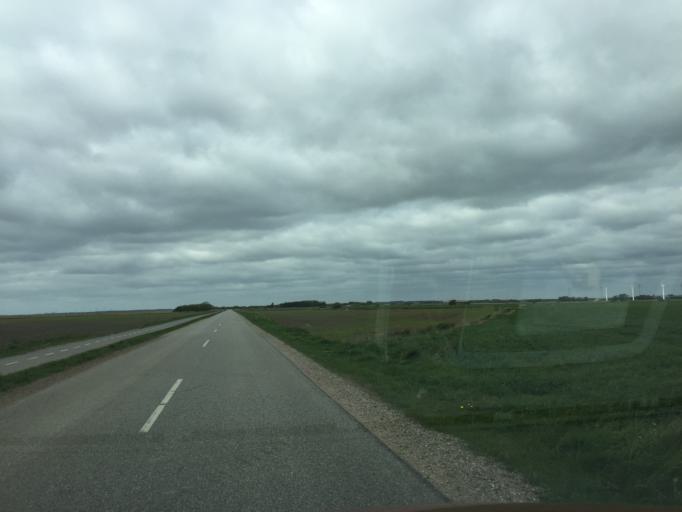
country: DK
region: Central Jutland
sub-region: Ringkobing-Skjern Kommune
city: Ringkobing
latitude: 56.0115
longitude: 8.3133
